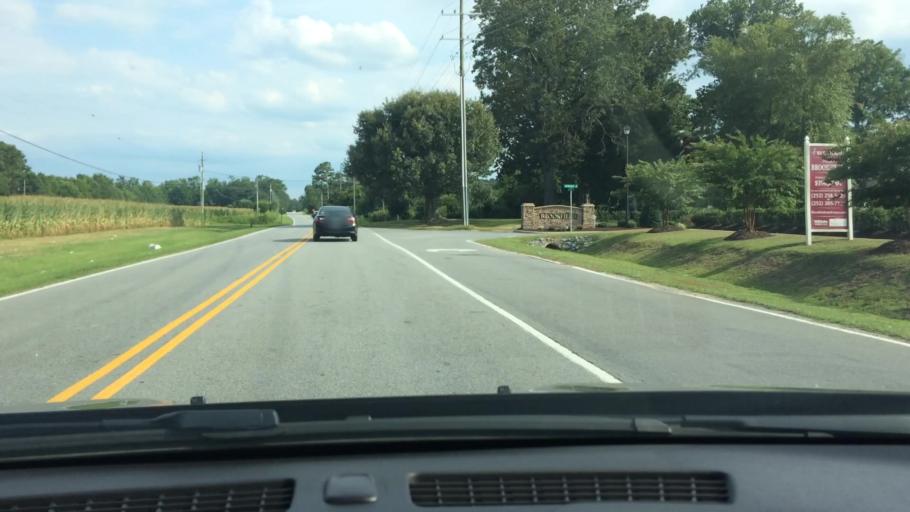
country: US
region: North Carolina
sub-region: Pitt County
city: Winterville
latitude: 35.5203
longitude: -77.3849
